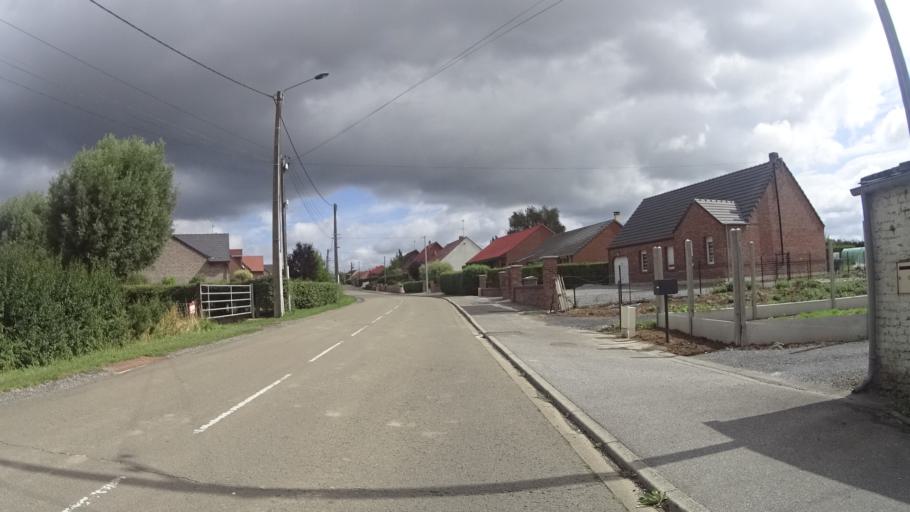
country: FR
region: Nord-Pas-de-Calais
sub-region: Departement du Nord
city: Landrecies
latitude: 50.1162
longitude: 3.6871
